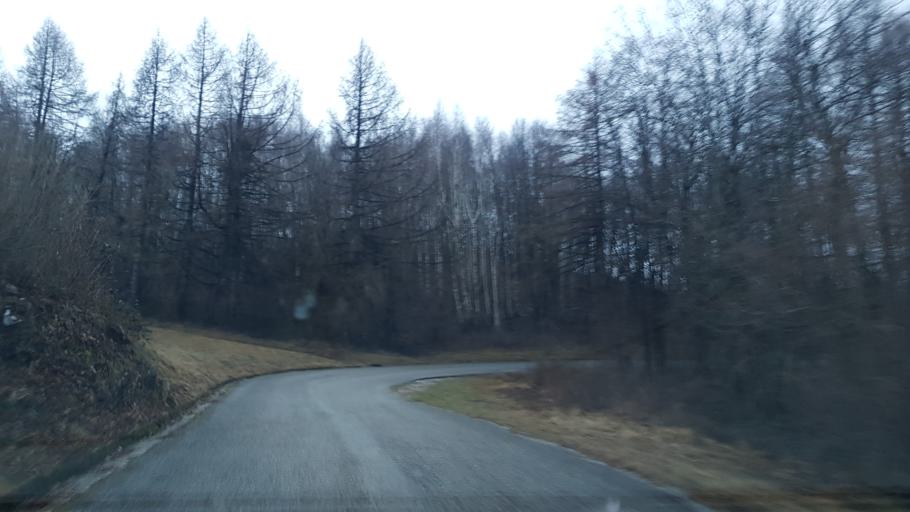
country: IT
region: Friuli Venezia Giulia
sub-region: Provincia di Udine
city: Stregna
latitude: 46.1061
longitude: 13.5630
